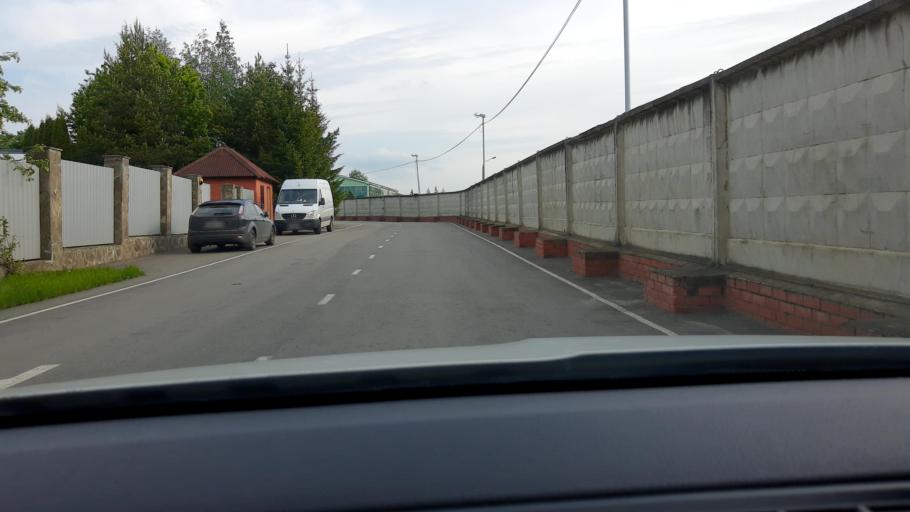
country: RU
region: Moskovskaya
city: Vatutinki
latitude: 55.5127
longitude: 37.3787
